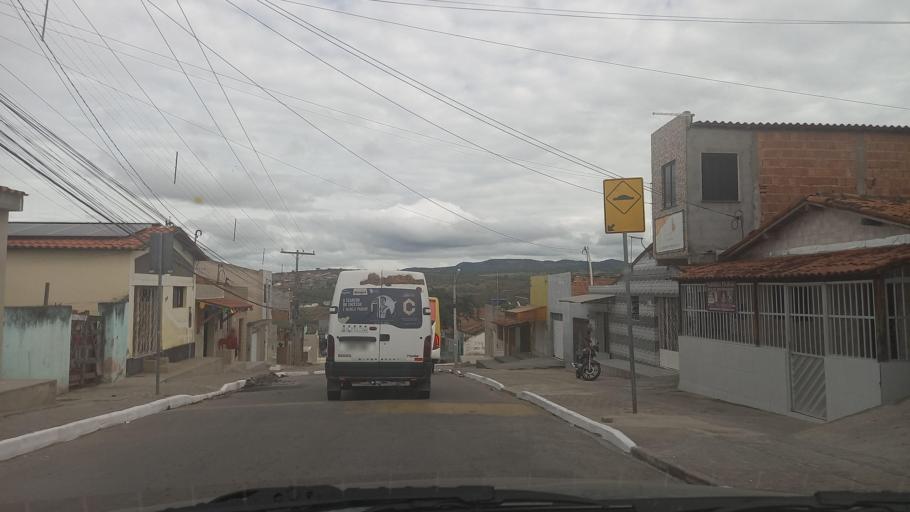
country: BR
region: Pernambuco
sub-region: Caruaru
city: Caruaru
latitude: -8.2948
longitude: -36.0301
